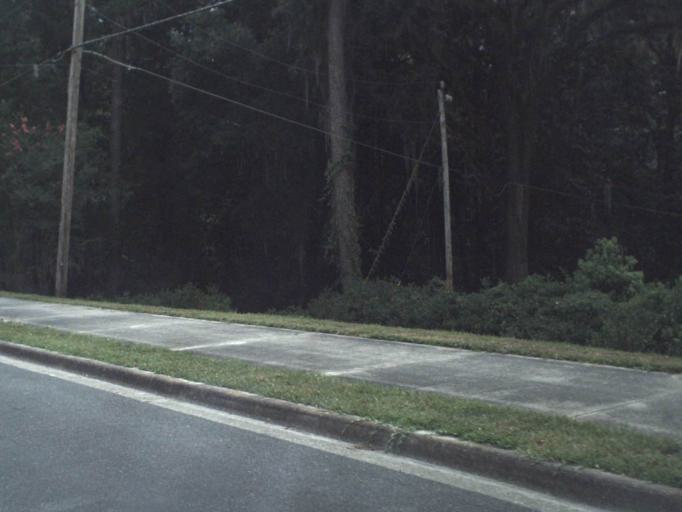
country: US
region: Florida
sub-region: Columbia County
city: Lake City
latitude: 30.1599
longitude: -82.6389
